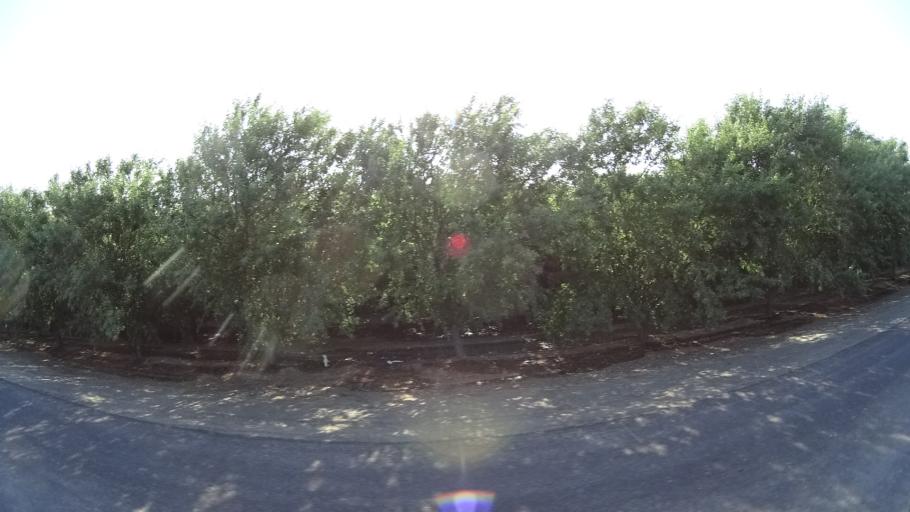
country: US
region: California
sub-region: Fresno County
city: Riverdale
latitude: 36.3697
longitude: -119.8161
